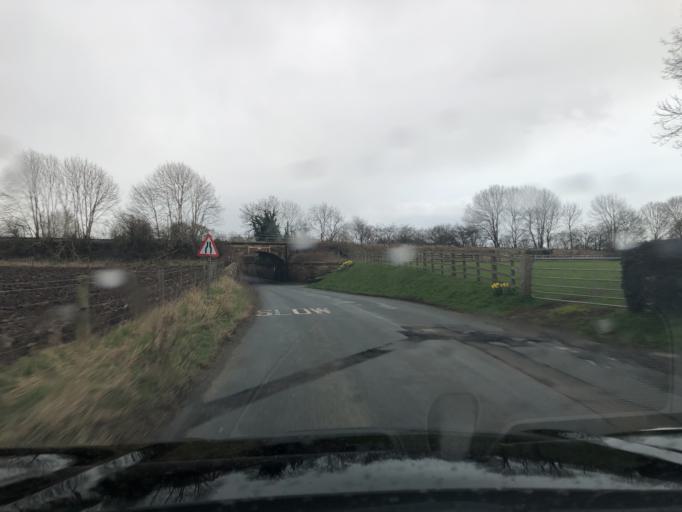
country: GB
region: England
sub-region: North Yorkshire
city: Northallerton
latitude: 54.3391
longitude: -1.4522
